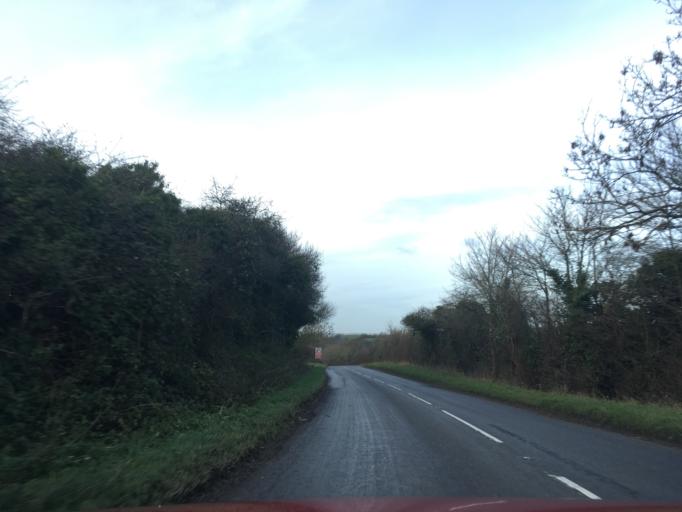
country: GB
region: England
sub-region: South Gloucestershire
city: Almondsbury
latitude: 51.5673
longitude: -2.5653
